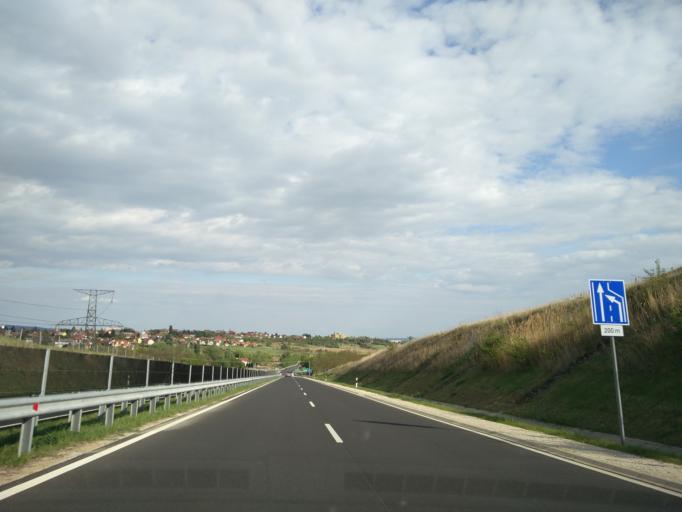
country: HU
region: Zala
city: Heviz
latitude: 46.7910
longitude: 17.1657
